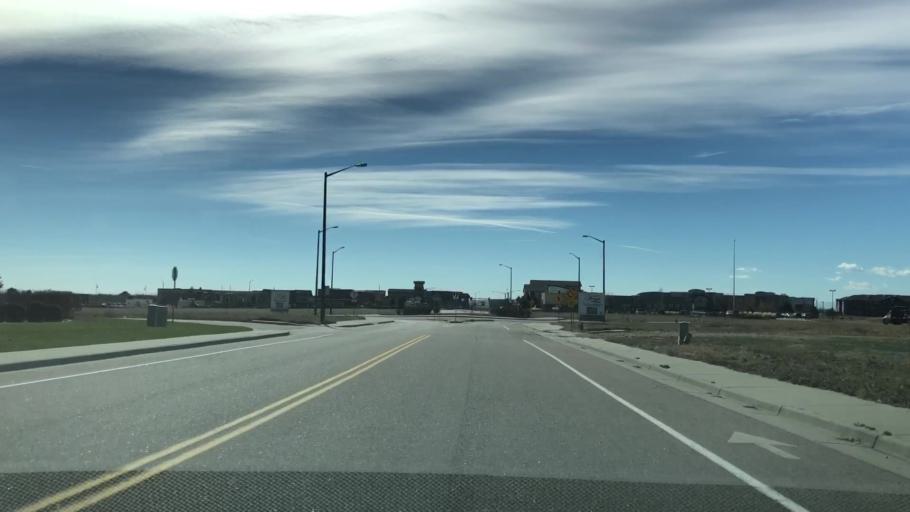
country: US
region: Colorado
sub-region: Weld County
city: Windsor
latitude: 40.4389
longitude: -104.9880
